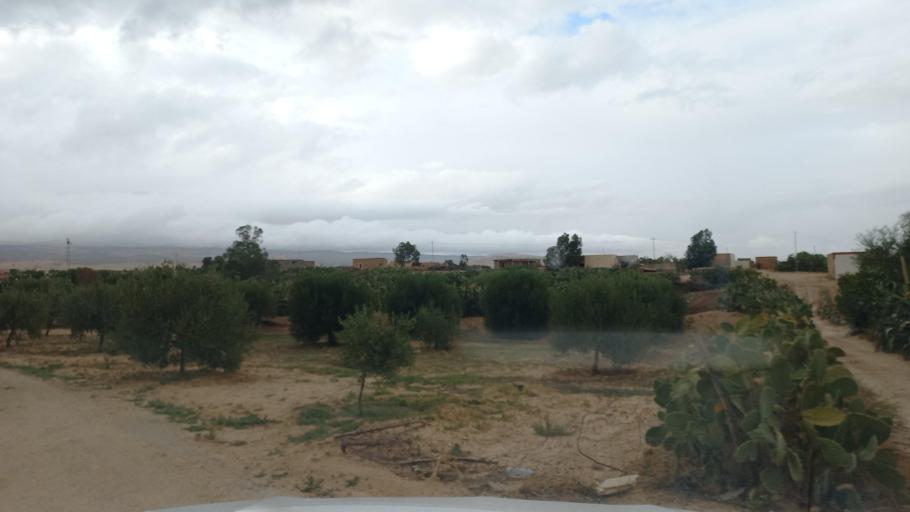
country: TN
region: Al Qasrayn
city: Kasserine
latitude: 35.2774
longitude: 8.9512
